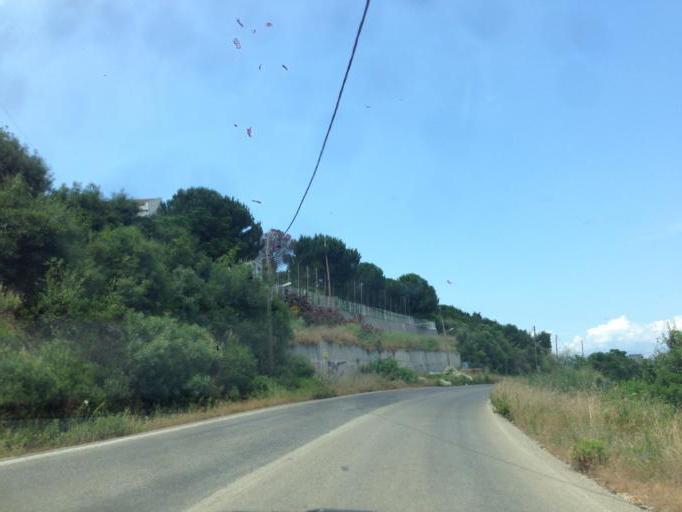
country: GR
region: Ionian Islands
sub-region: Nomos Kerkyras
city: Acharavi
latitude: 39.7889
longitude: 19.9089
